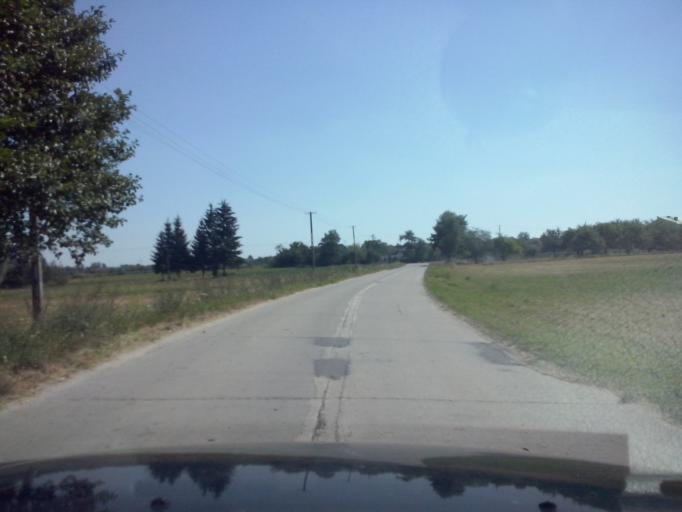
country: PL
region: Swietokrzyskie
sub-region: Powiat buski
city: Gnojno
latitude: 50.5949
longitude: 20.8162
